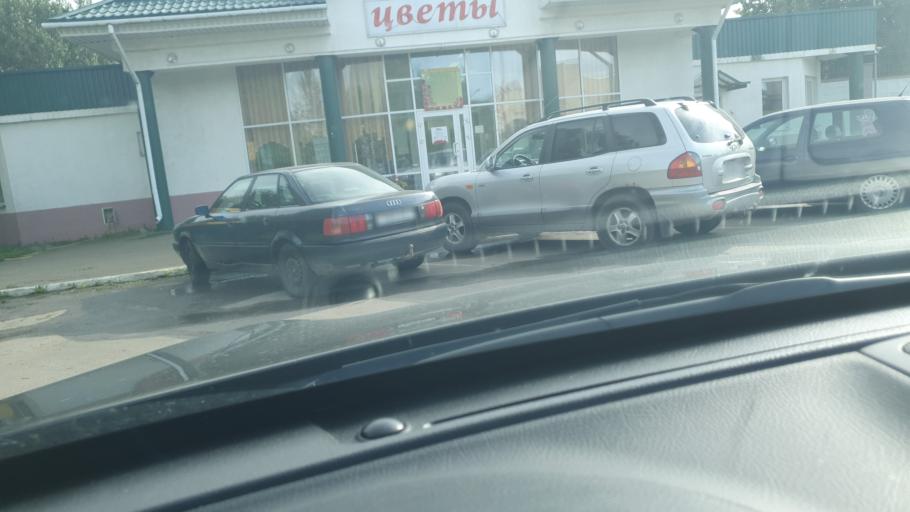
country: BY
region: Minsk
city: Azyartso
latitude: 53.8679
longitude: 27.3955
